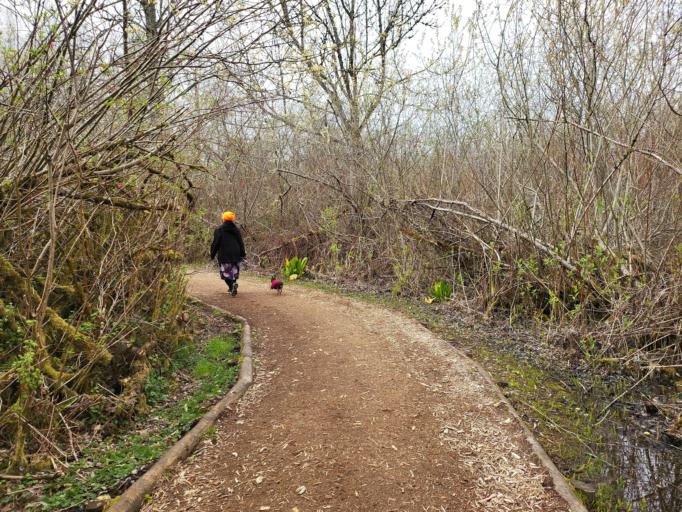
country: US
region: Washington
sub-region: King County
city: Newport
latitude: 47.5915
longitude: -122.1850
